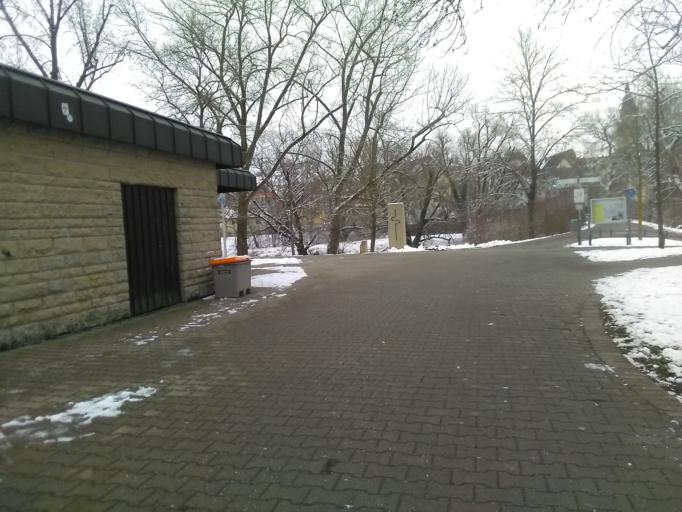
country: DE
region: Baden-Wuerttemberg
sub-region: Regierungsbezirk Stuttgart
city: Crailsheim
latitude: 49.1373
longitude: 10.0675
